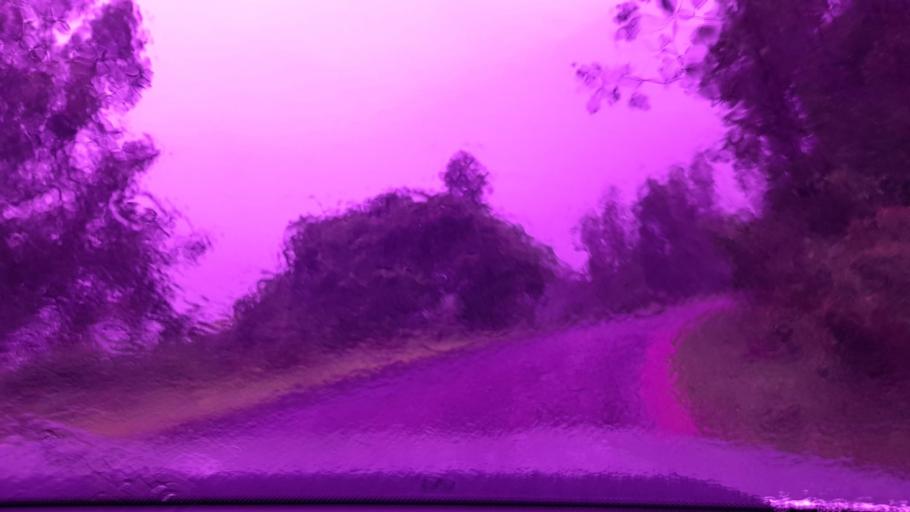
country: ET
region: Oromiya
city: Metu
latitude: 8.4705
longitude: 35.6381
